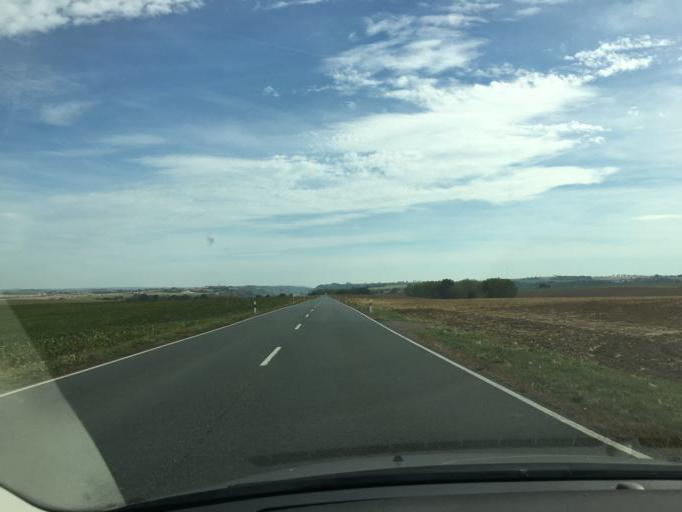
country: DE
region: Saxony
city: Lommatzsch
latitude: 51.2097
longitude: 13.3805
